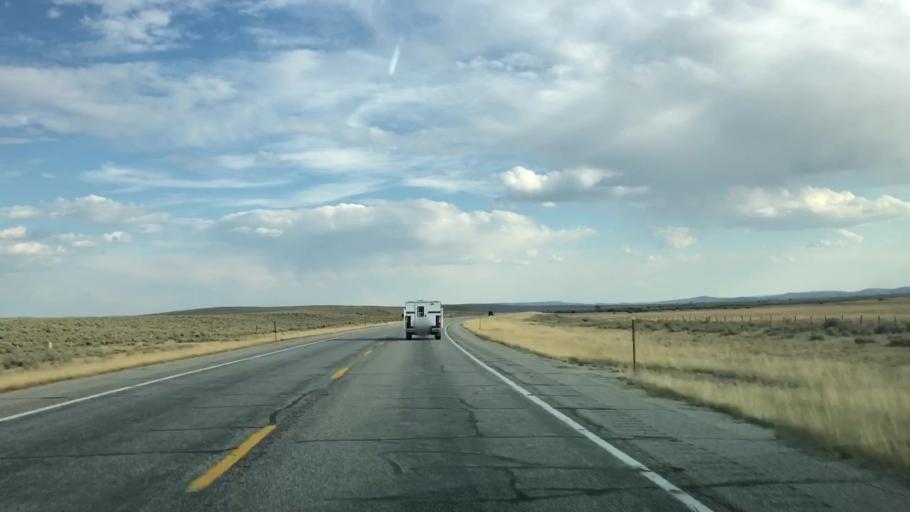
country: US
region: Wyoming
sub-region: Sublette County
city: Pinedale
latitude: 43.0318
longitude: -110.1283
